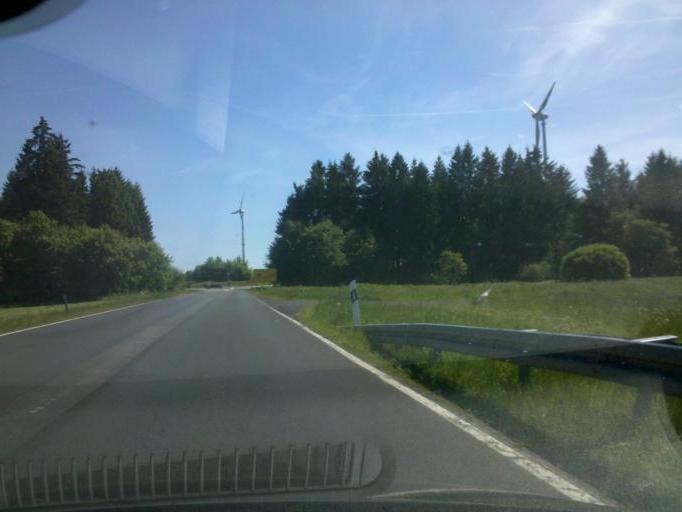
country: DE
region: Rheinland-Pfalz
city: Rehe
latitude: 50.6507
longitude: 8.1384
